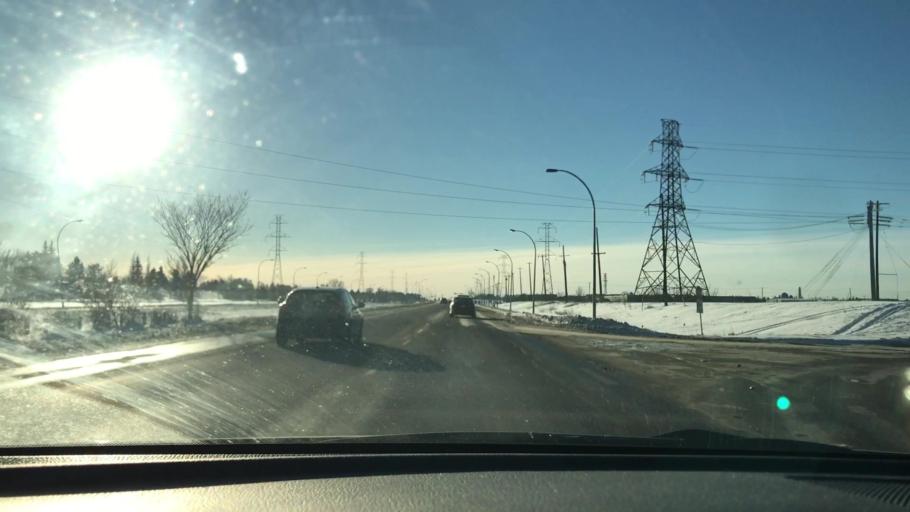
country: CA
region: Alberta
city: Edmonton
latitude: 53.4630
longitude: -113.4668
